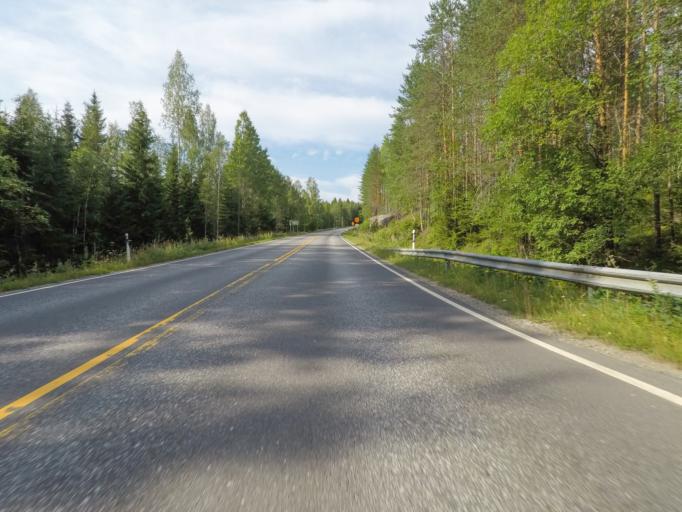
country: FI
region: Southern Savonia
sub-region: Savonlinna
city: Sulkava
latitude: 61.8554
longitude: 28.4663
